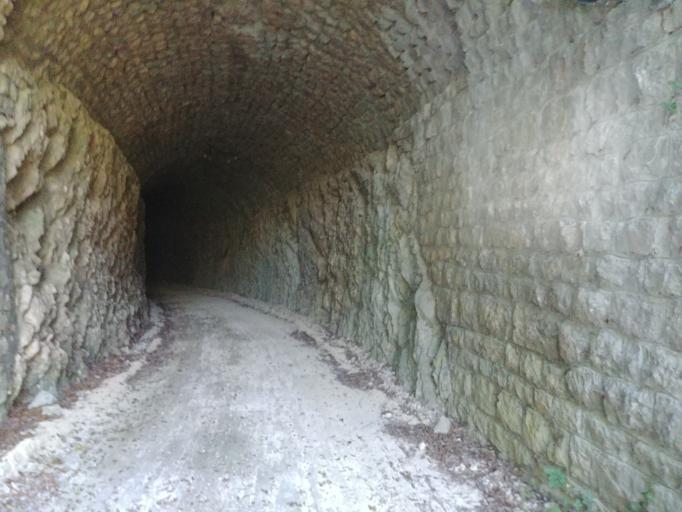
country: IT
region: Umbria
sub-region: Provincia di Perugia
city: Sant'Anatolia di Narco
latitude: 42.7477
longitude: 12.8203
